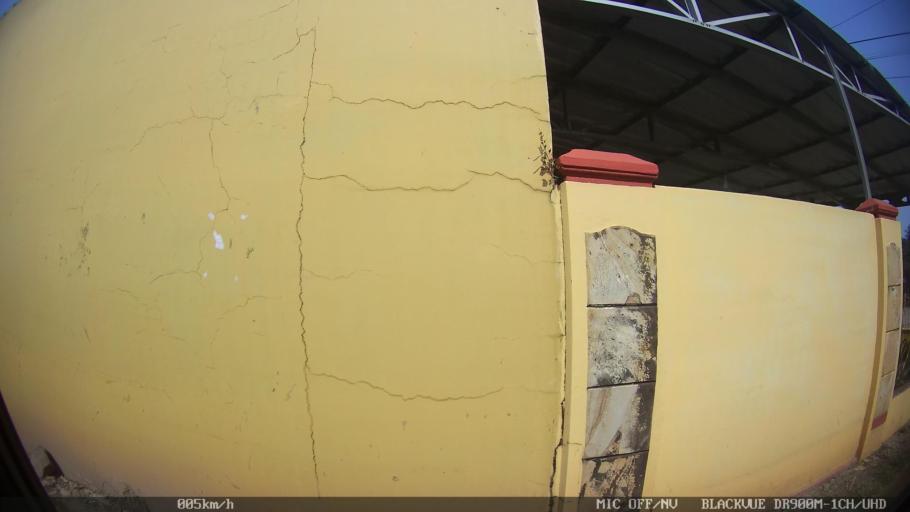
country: ID
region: Lampung
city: Natar
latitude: -5.3151
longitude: 105.2040
